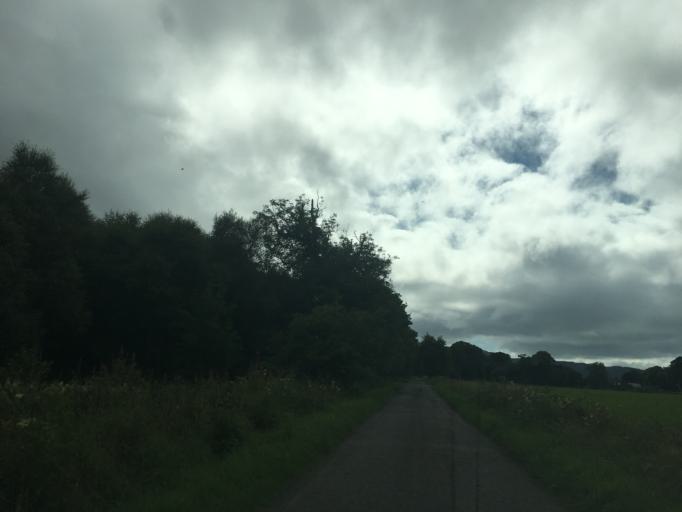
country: GB
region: Scotland
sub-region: Argyll and Bute
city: Lochgilphead
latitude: 56.1056
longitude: -5.4996
